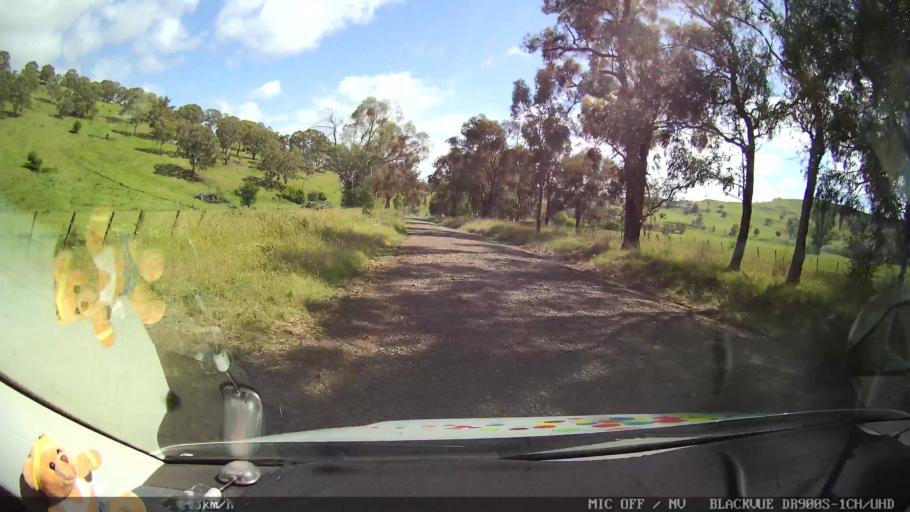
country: AU
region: New South Wales
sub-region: Guyra
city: Guyra
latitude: -29.9849
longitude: 151.6941
